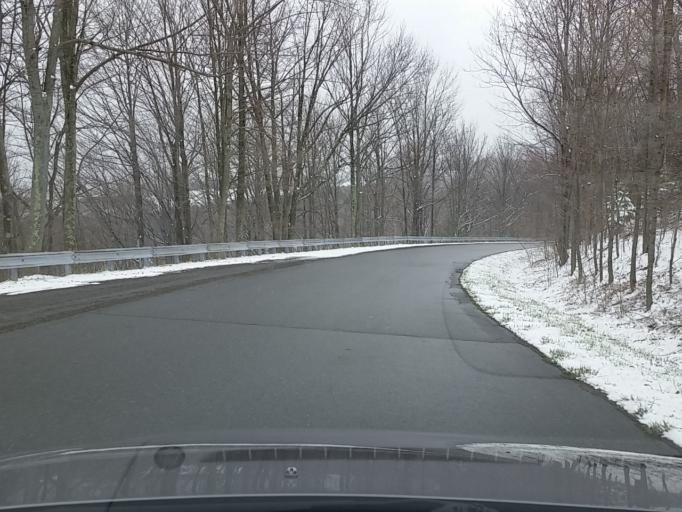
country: US
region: Pennsylvania
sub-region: Sullivan County
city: Laporte
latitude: 41.3778
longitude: -76.5174
